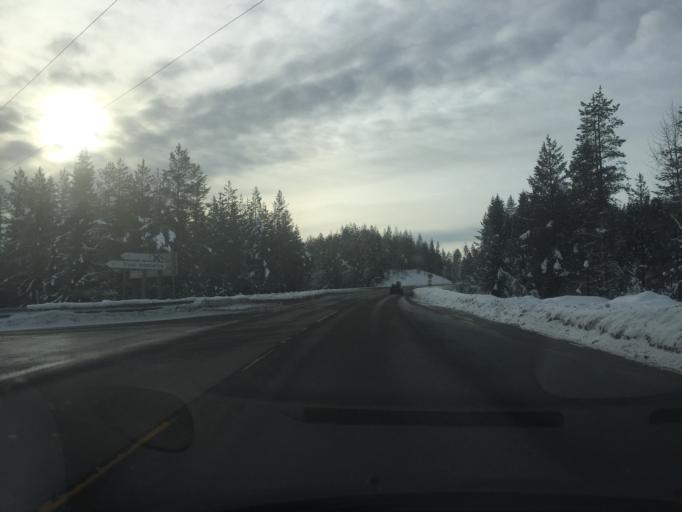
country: NO
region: Hedmark
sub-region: Trysil
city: Innbygda
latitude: 61.2621
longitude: 12.3082
